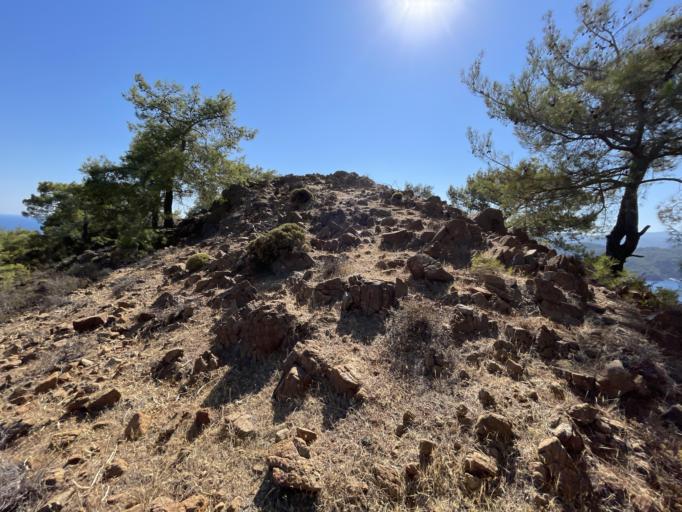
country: TR
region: Mugla
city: Goecek
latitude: 36.7305
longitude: 28.9627
